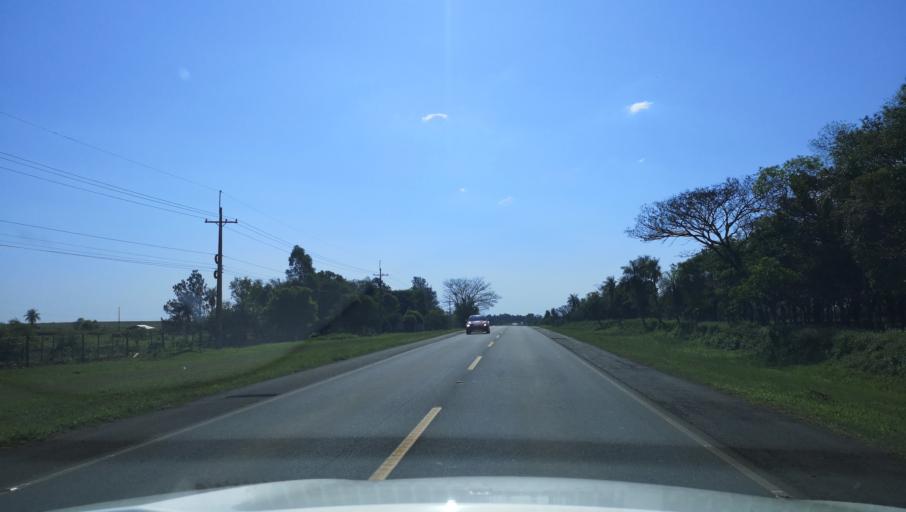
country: PY
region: Misiones
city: San Patricio
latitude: -27.0279
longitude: -56.6966
